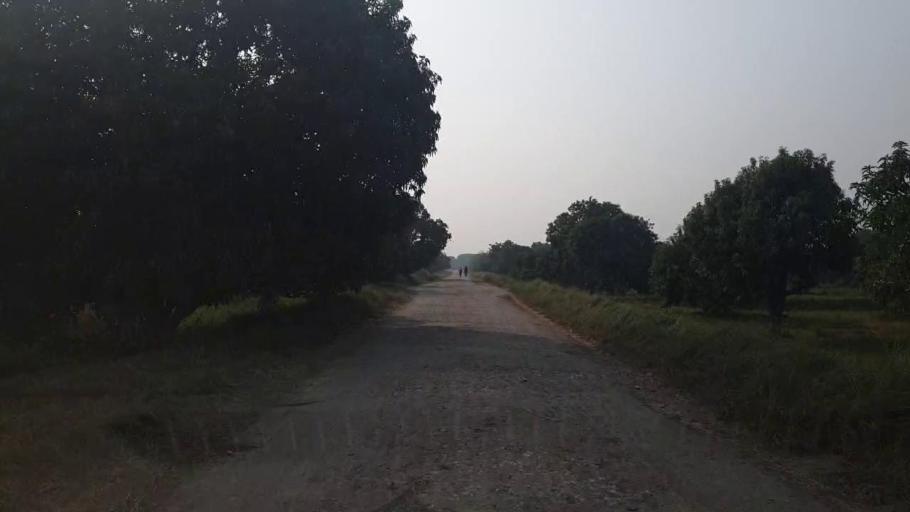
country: PK
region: Sindh
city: Tando Jam
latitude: 25.3283
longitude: 68.5180
